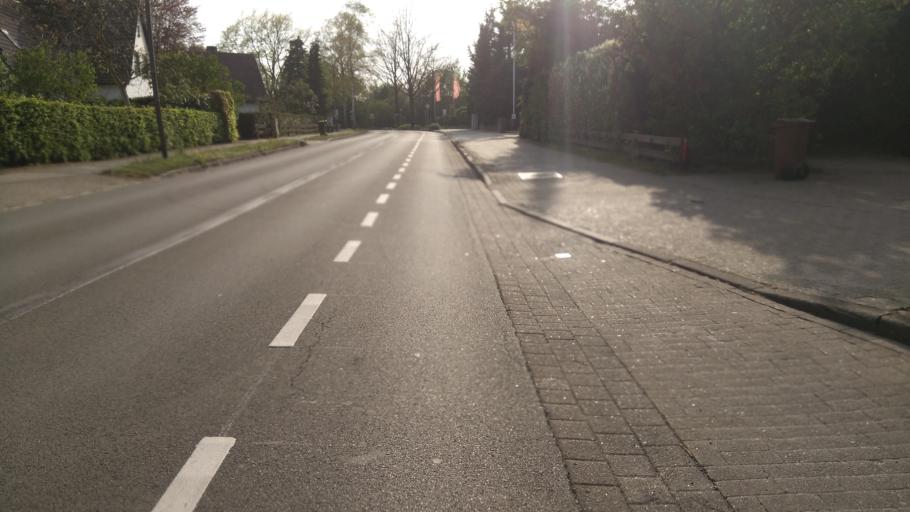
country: DE
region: Lower Saxony
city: Buxtehude
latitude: 53.4601
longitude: 9.6740
